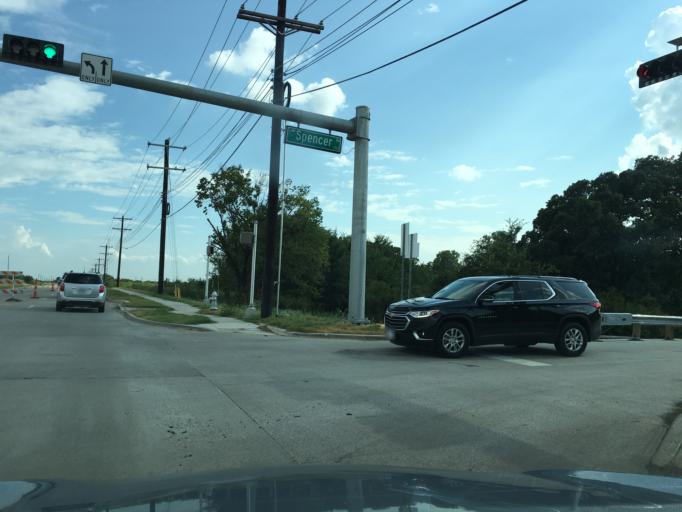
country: US
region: Texas
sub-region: Denton County
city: Corinth
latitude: 33.1956
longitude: -97.0853
